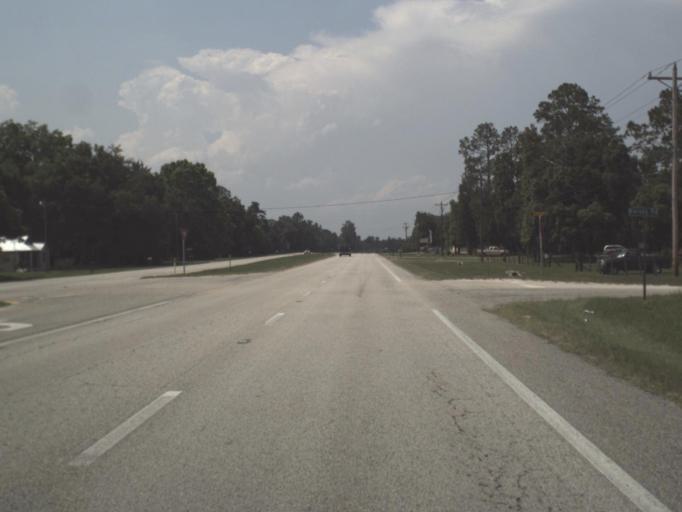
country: US
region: Florida
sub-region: Clay County
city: Green Cove Springs
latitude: 29.9286
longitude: -81.6863
